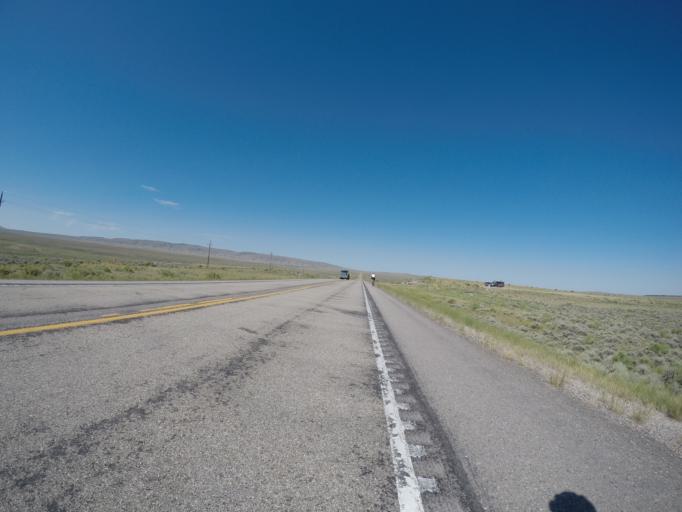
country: US
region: Wyoming
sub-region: Carbon County
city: Saratoga
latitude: 41.8235
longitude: -106.6477
